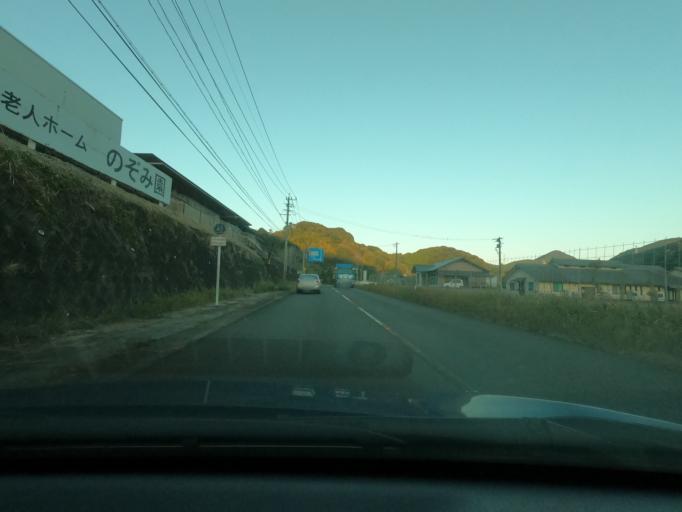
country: JP
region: Kagoshima
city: Satsumasendai
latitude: 31.8089
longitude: 130.4848
